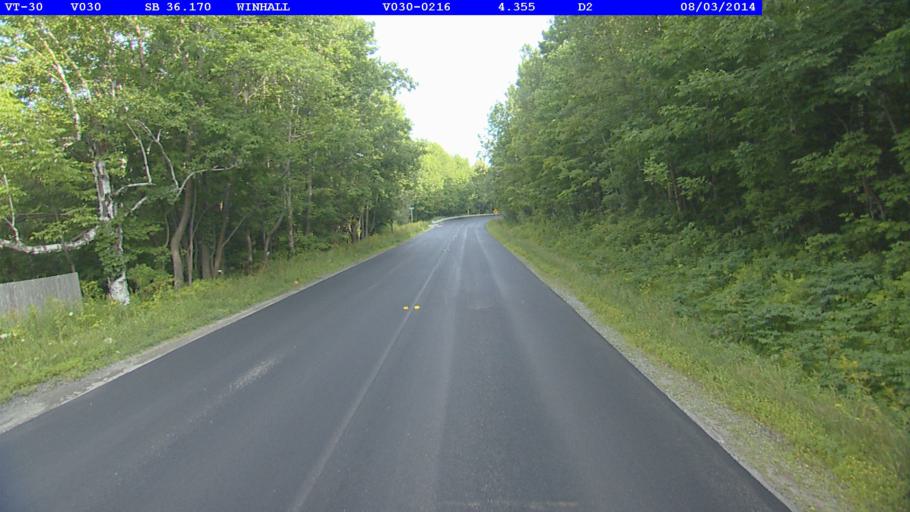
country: US
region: Vermont
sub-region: Bennington County
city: Manchester Center
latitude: 43.1727
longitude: -72.9229
